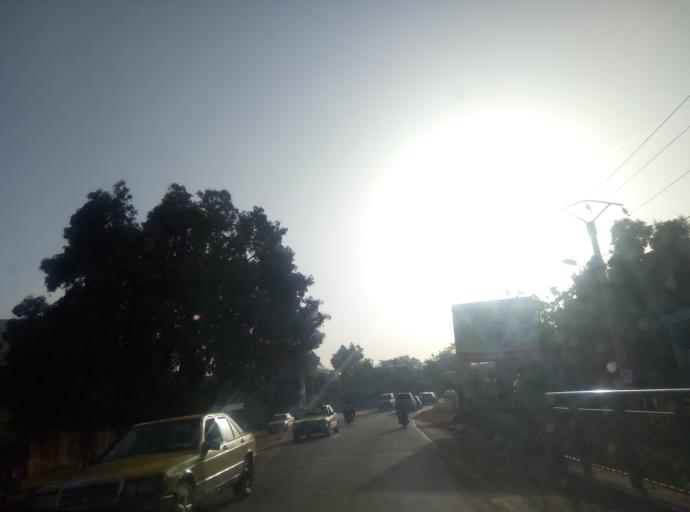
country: ML
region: Bamako
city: Bamako
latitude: 12.6111
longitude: -7.9745
